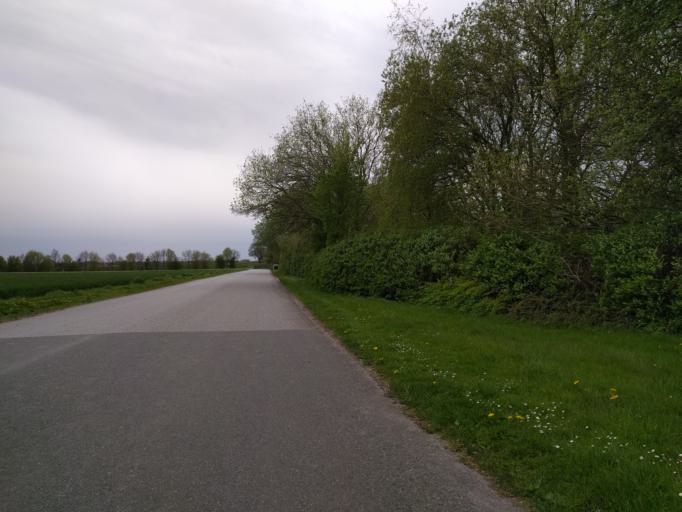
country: DK
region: South Denmark
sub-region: Kerteminde Kommune
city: Munkebo
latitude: 55.4668
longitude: 10.5915
